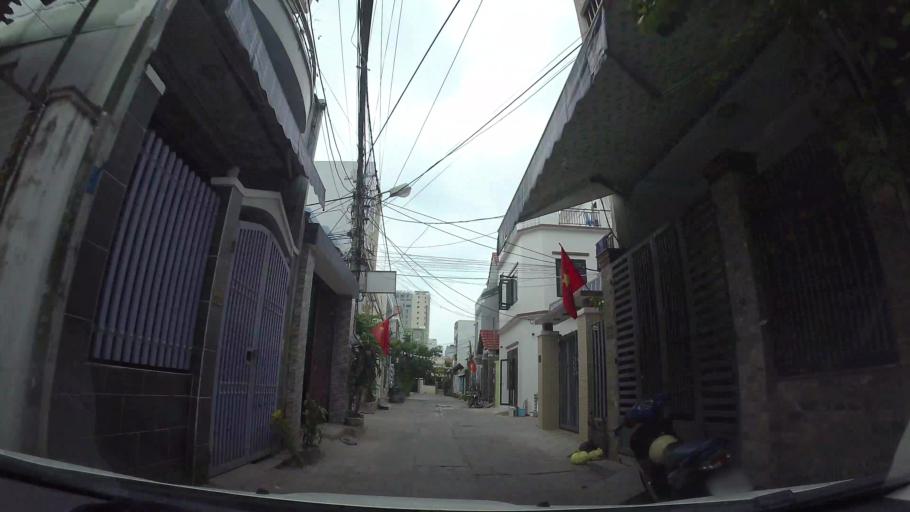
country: VN
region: Da Nang
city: Son Tra
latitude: 16.0596
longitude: 108.2381
